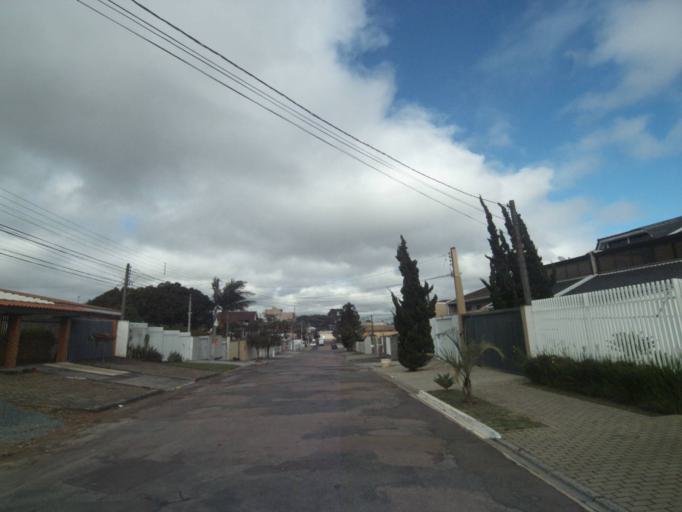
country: BR
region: Parana
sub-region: Sao Jose Dos Pinhais
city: Sao Jose dos Pinhais
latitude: -25.5221
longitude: -49.2985
